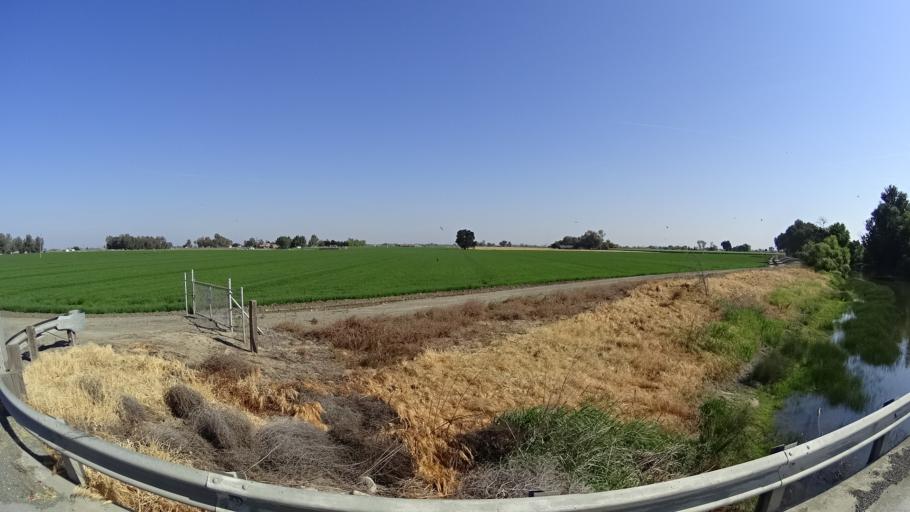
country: US
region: California
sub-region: Fresno County
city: Riverdale
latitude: 36.3437
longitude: -119.8625
